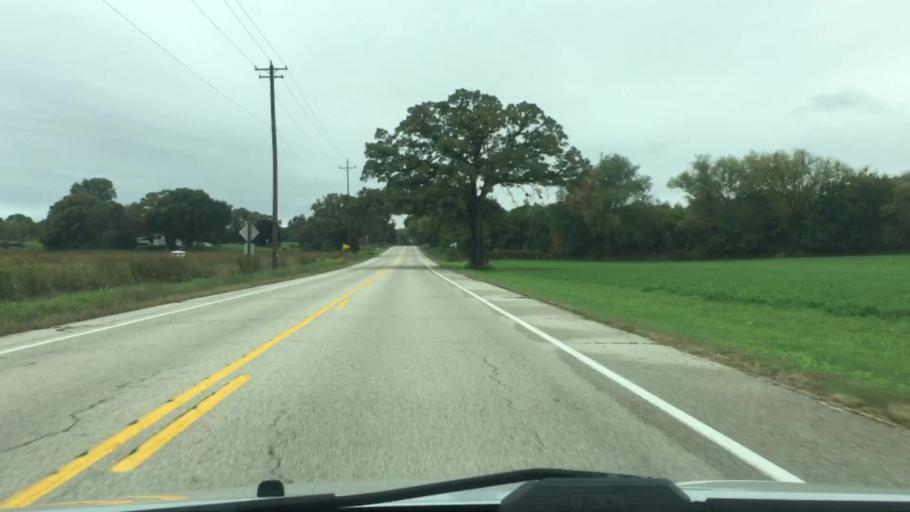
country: US
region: Wisconsin
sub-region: Waukesha County
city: Eagle
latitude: 42.8545
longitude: -88.5111
